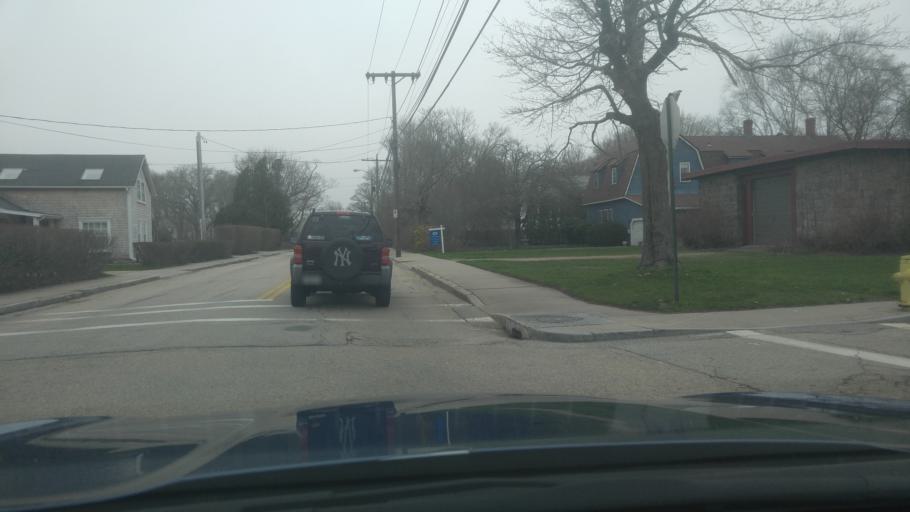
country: US
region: Rhode Island
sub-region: Washington County
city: Narragansett Pier
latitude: 41.4273
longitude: -71.4593
